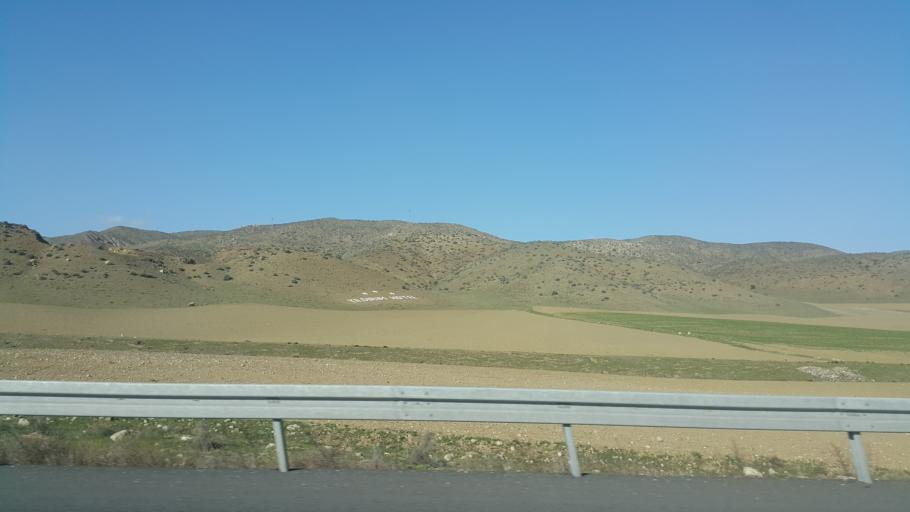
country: TR
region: Ankara
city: Sereflikochisar
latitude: 38.8125
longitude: 33.6066
